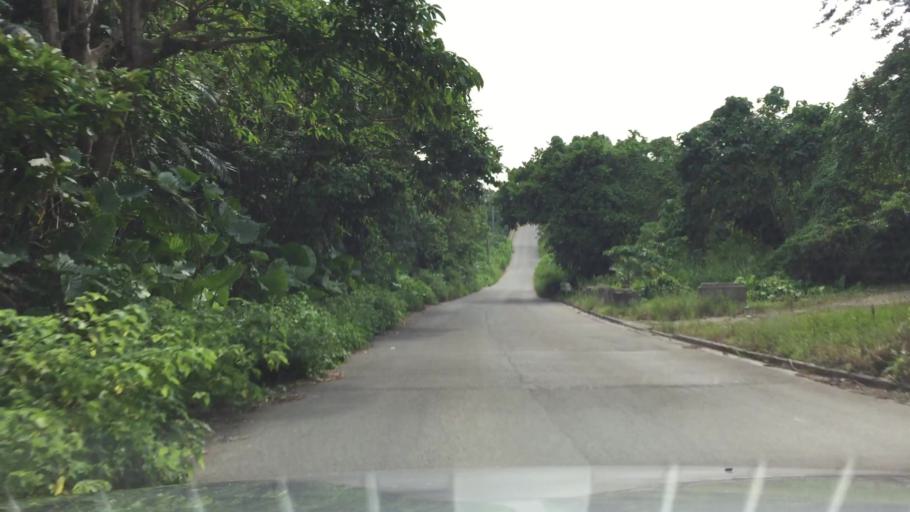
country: JP
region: Okinawa
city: Ishigaki
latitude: 24.3989
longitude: 124.2018
